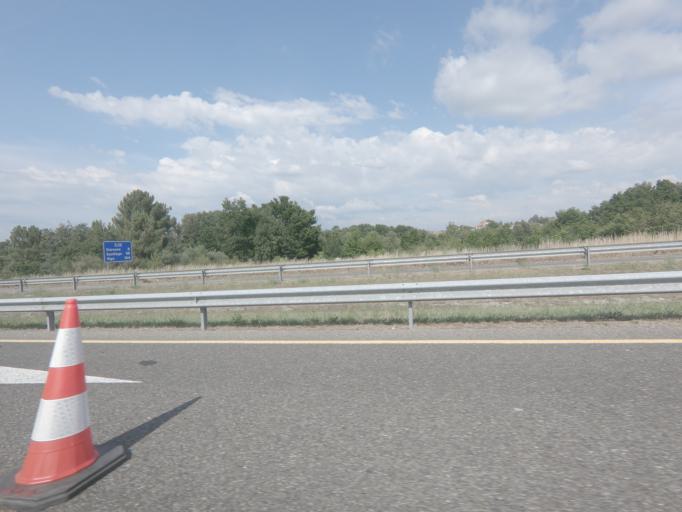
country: ES
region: Galicia
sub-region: Provincia de Ourense
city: Taboadela
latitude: 42.2547
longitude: -7.8689
